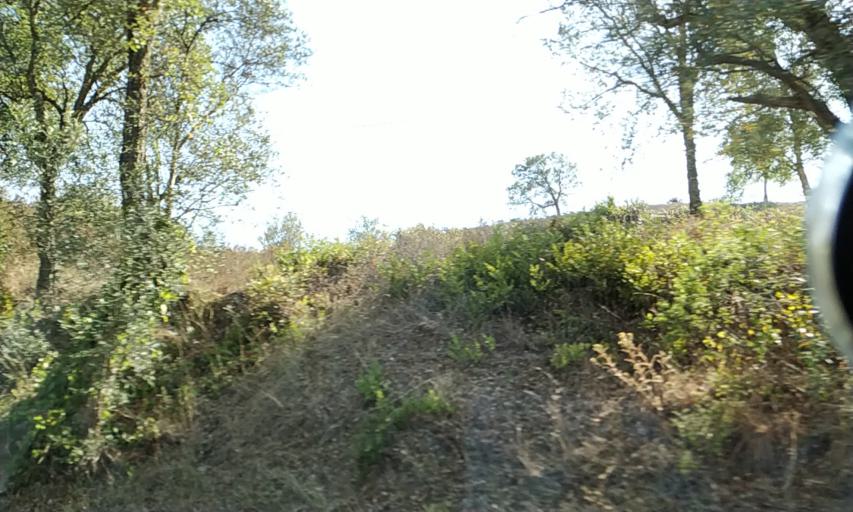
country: PT
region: Santarem
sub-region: Benavente
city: Poceirao
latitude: 38.7662
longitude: -8.6206
